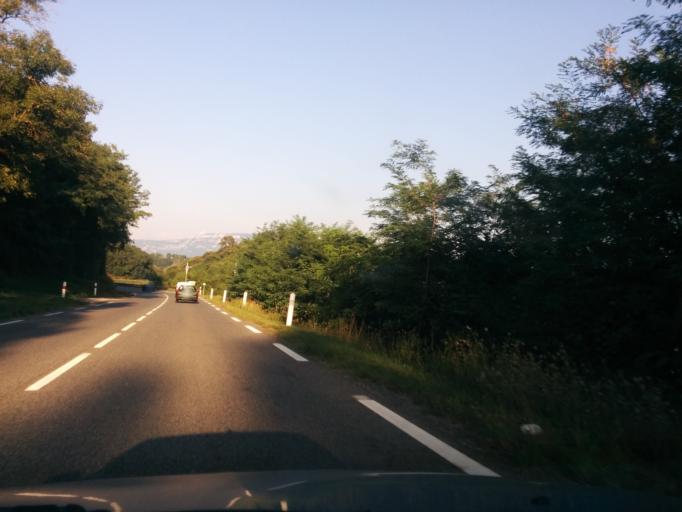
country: FR
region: Rhone-Alpes
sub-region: Departement de l'Isere
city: Les Abrets
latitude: 45.5312
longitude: 5.6161
